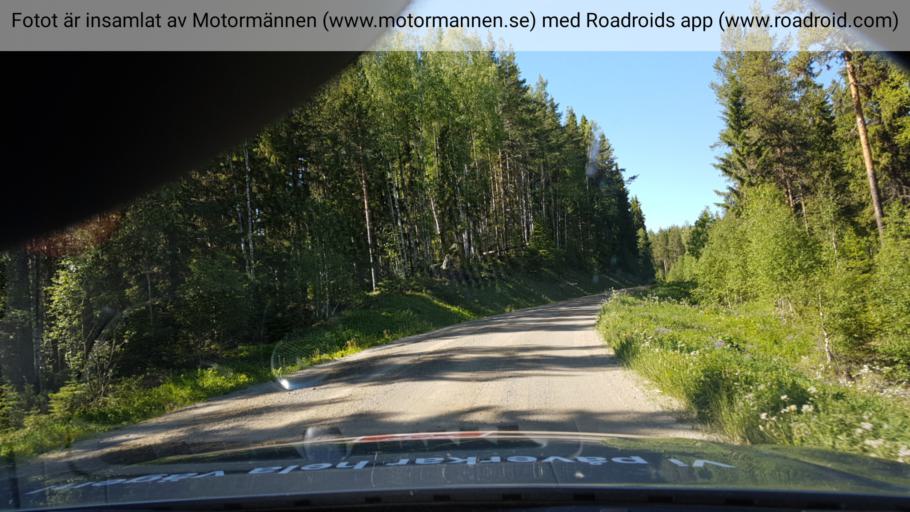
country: SE
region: Jaemtland
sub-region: OEstersunds Kommun
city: Brunflo
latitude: 62.9471
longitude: 14.9453
